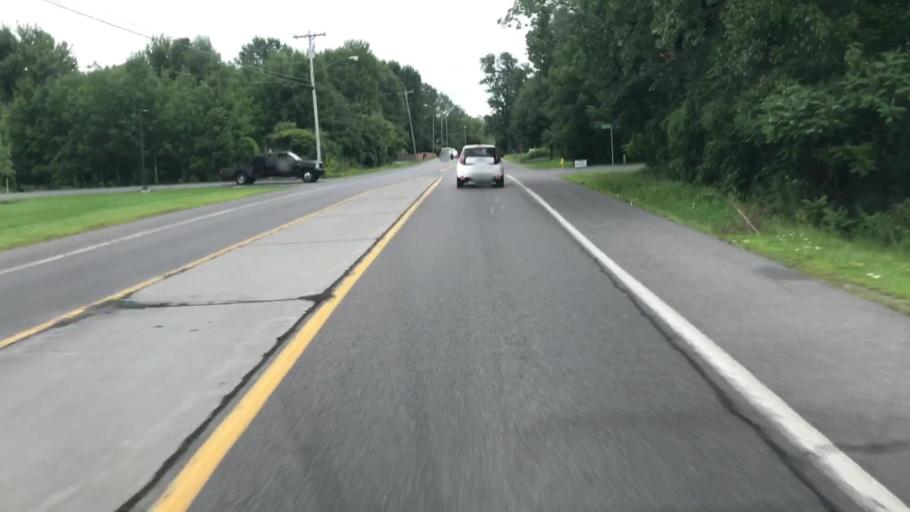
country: US
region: New York
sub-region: Onondaga County
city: North Syracuse
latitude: 43.1360
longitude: -76.1697
